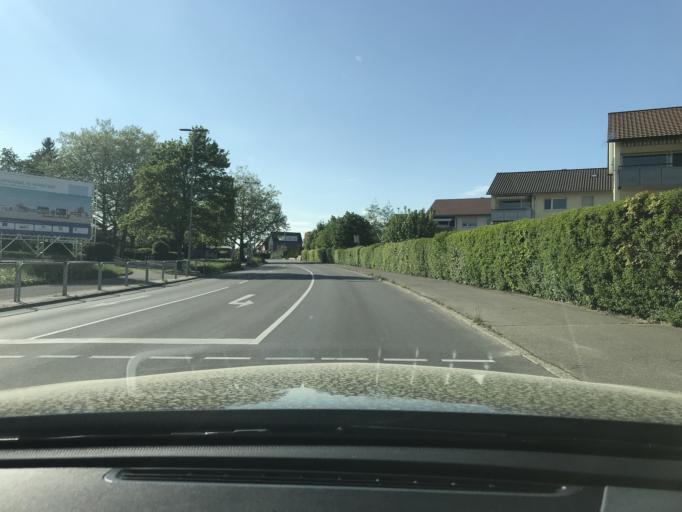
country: DE
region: Baden-Wuerttemberg
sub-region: Regierungsbezirk Stuttgart
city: Weinstadt-Endersbach
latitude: 48.8096
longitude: 9.3754
